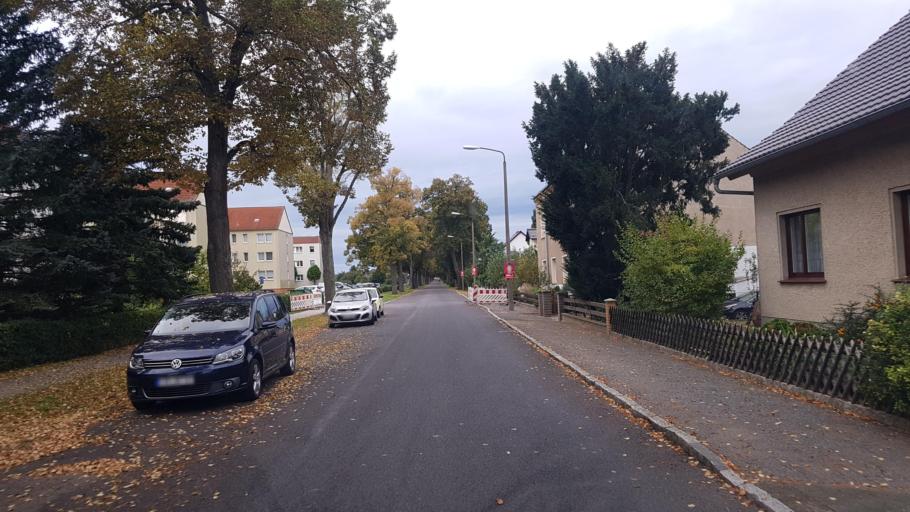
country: DE
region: Brandenburg
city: Golssen
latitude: 51.9731
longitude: 13.5904
